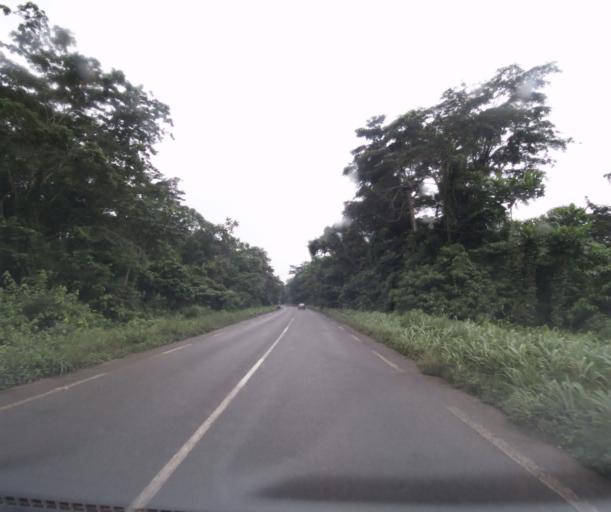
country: CM
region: Centre
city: Eseka
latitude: 3.8927
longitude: 10.7252
